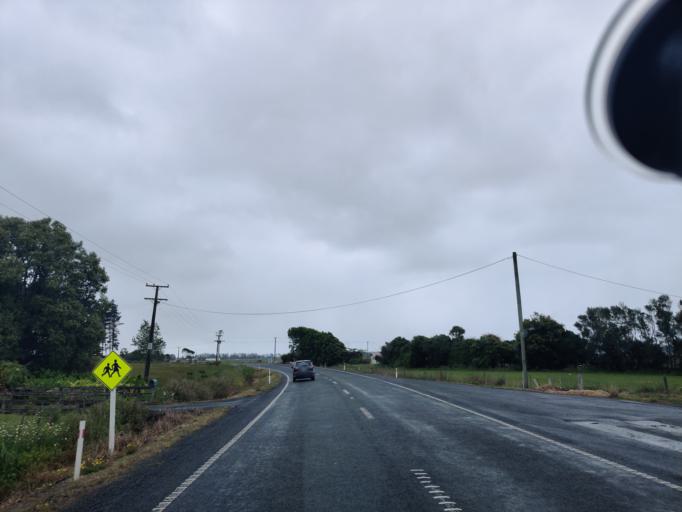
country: NZ
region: Northland
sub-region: Kaipara District
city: Dargaville
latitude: -35.9950
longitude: 173.9196
